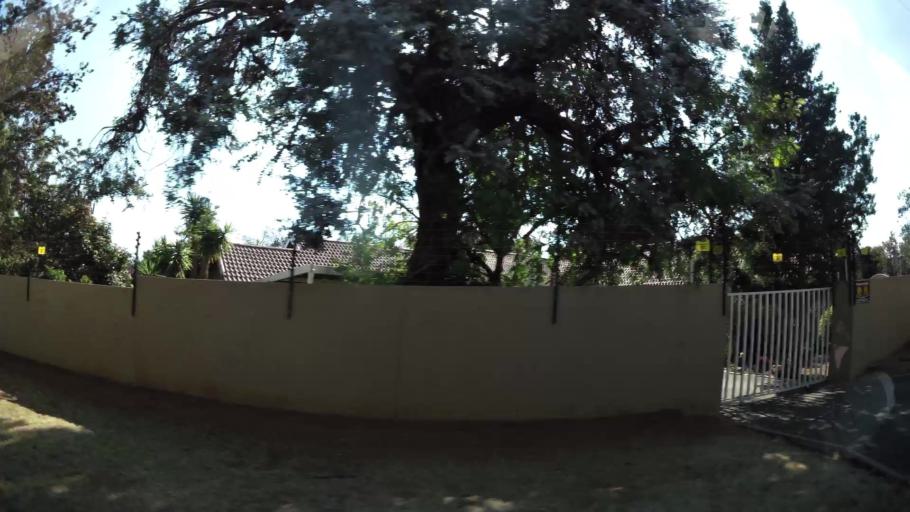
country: ZA
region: Gauteng
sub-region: West Rand District Municipality
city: Randfontein
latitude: -26.1519
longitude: 27.7013
